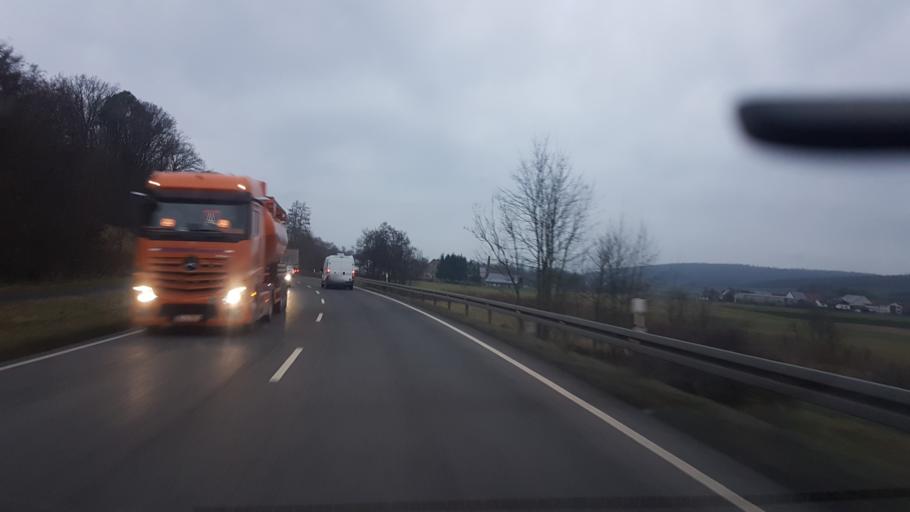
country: DE
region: Bavaria
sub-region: Regierungsbezirk Unterfranken
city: Rentweinsdorf
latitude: 50.0555
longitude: 10.8109
